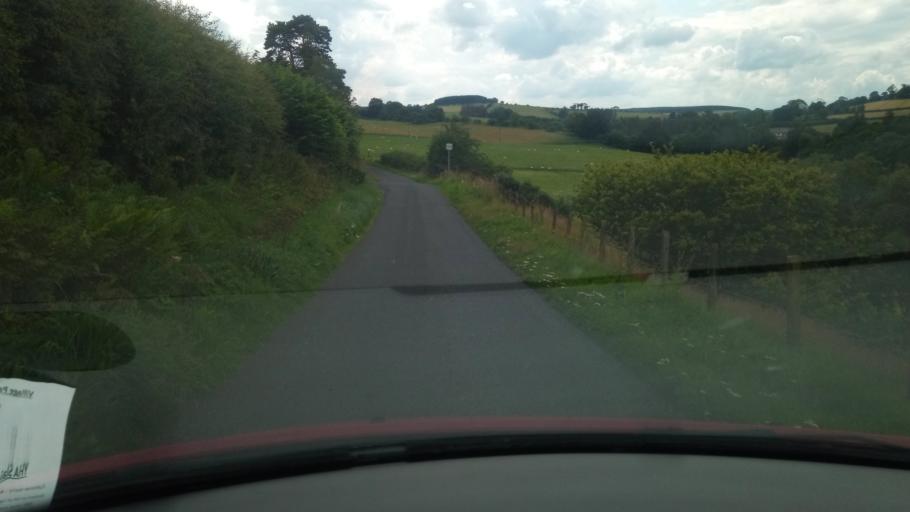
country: GB
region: Scotland
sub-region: The Scottish Borders
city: Jedburgh
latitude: 55.4046
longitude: -2.6478
